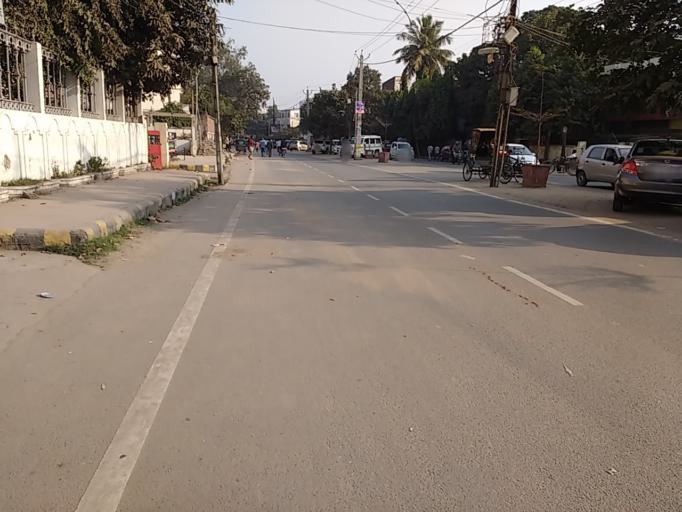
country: IN
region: Bihar
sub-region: Patna
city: Patna
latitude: 25.6122
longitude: 85.1152
